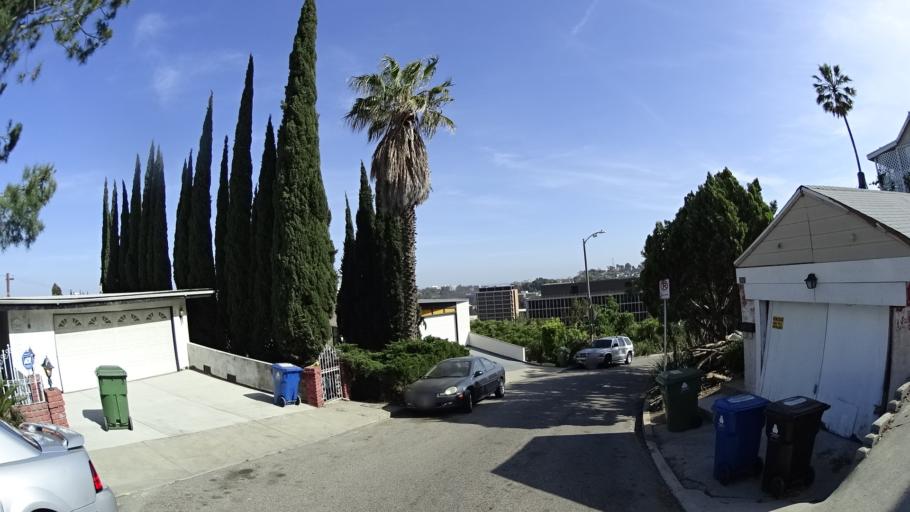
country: US
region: California
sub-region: Los Angeles County
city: Belvedere
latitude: 34.0677
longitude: -118.1707
